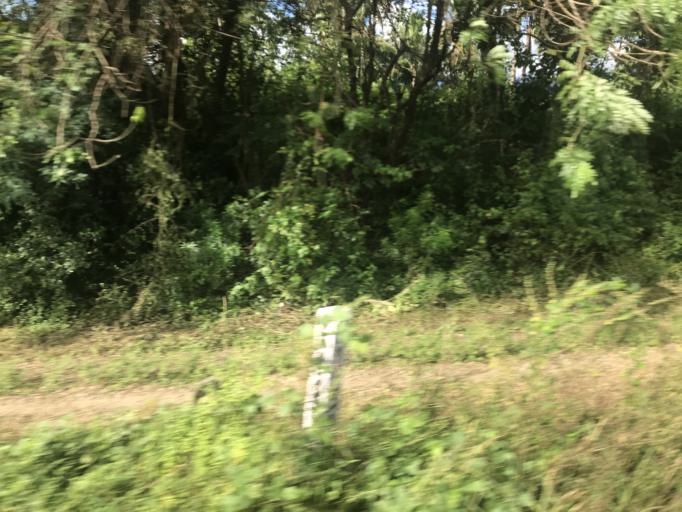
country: IN
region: Kerala
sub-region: Palakkad district
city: Palakkad
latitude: 10.8163
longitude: 76.6914
